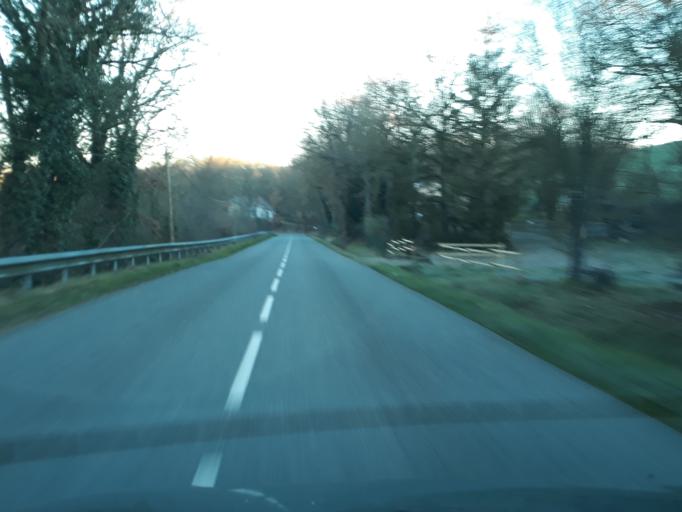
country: FR
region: Midi-Pyrenees
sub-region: Departement du Gers
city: Pavie
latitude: 43.6173
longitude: 0.6754
